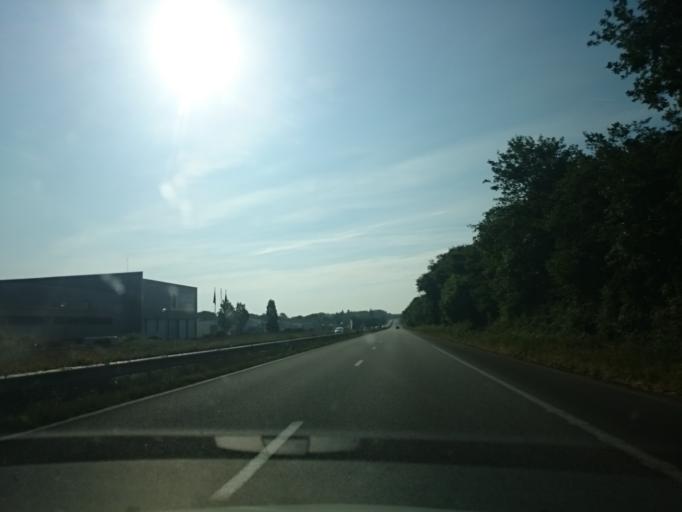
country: FR
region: Brittany
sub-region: Departement du Finistere
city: Ergue-Gaberic
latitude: 47.9704
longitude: -3.9965
